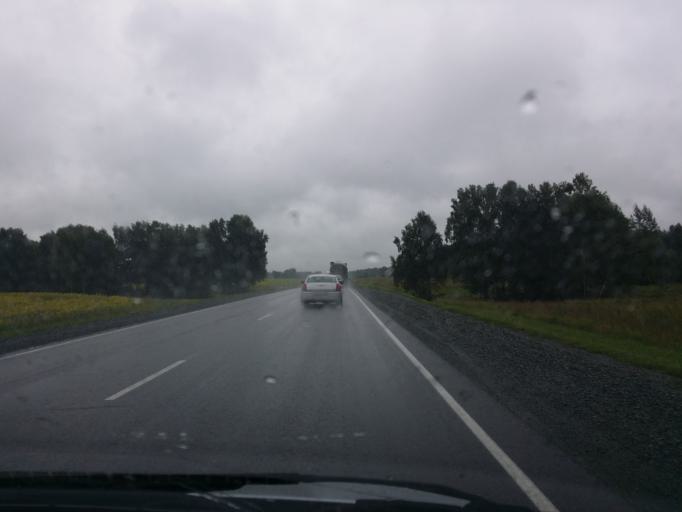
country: RU
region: Altai Krai
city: Bayunovskiye Klyuchi
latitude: 53.3138
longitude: 84.2233
